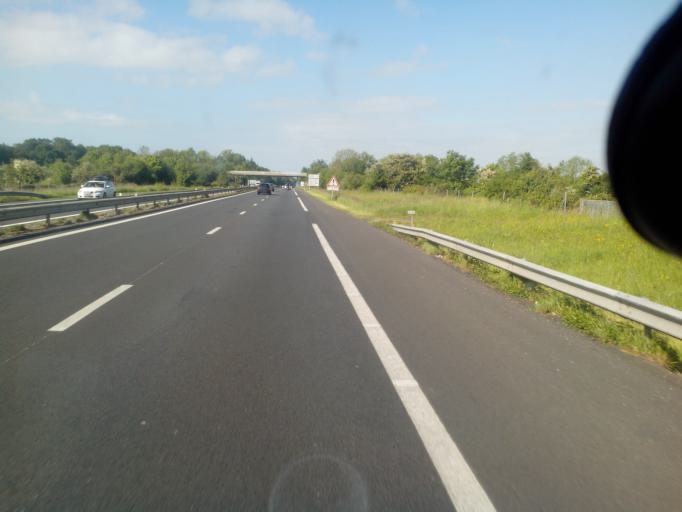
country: FR
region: Lower Normandy
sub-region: Departement du Calvados
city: Troarn
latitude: 49.1863
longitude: -0.1937
